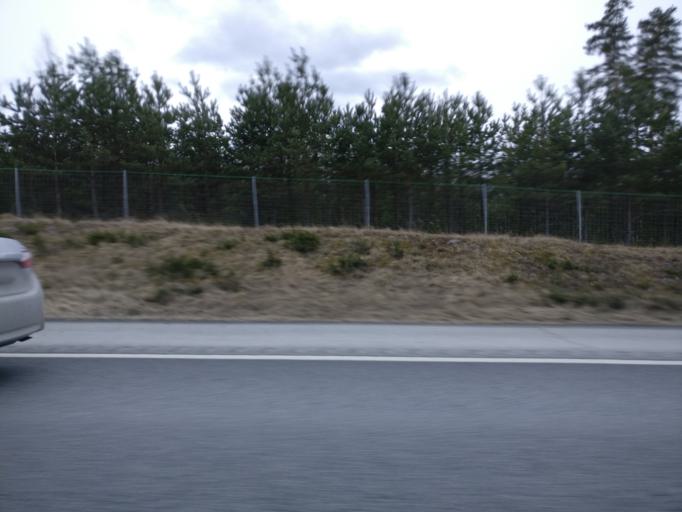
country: FI
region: Haeme
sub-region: Haemeenlinna
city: Kalvola
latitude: 61.1295
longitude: 24.1065
